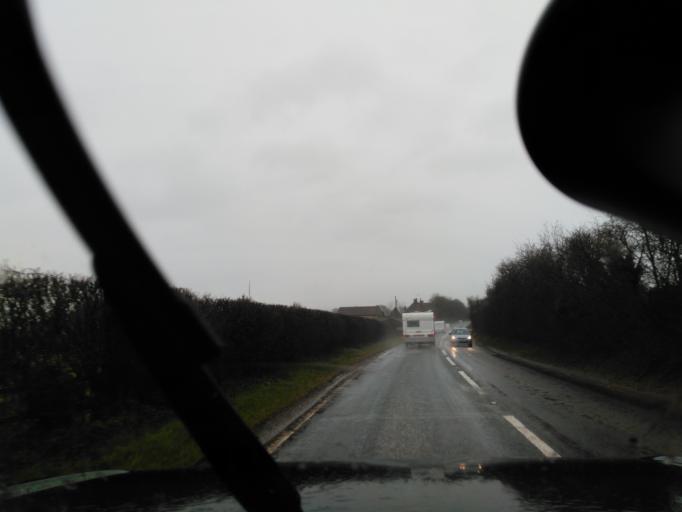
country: GB
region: England
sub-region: Somerset
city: Bruton
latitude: 51.1948
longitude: -2.4234
